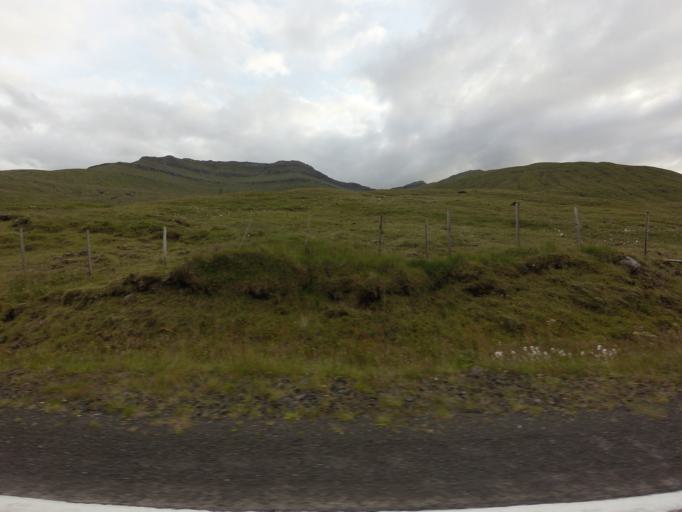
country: FO
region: Streymoy
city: Kollafjordhur
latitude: 62.1738
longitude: -6.9767
